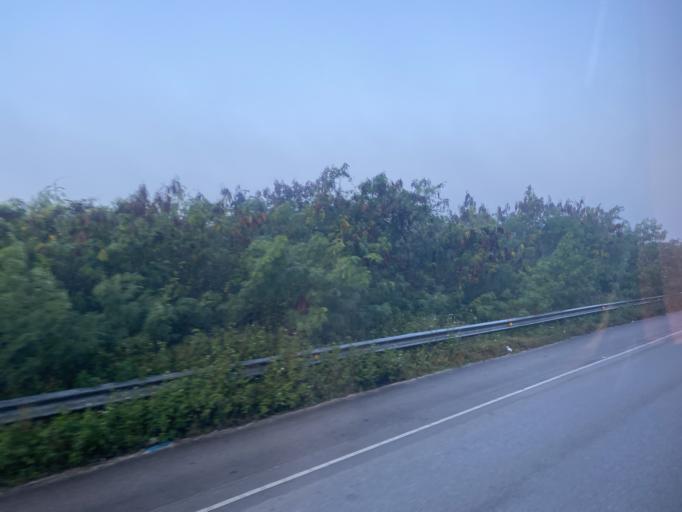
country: DO
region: La Altagracia
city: Otra Banda
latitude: 18.7362
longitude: -68.5102
